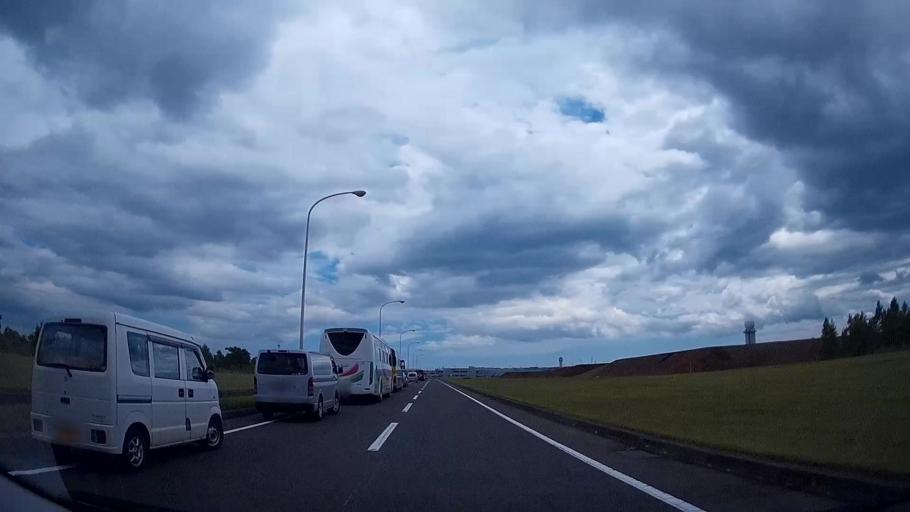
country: JP
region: Hokkaido
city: Chitose
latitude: 42.8005
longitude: 141.6798
